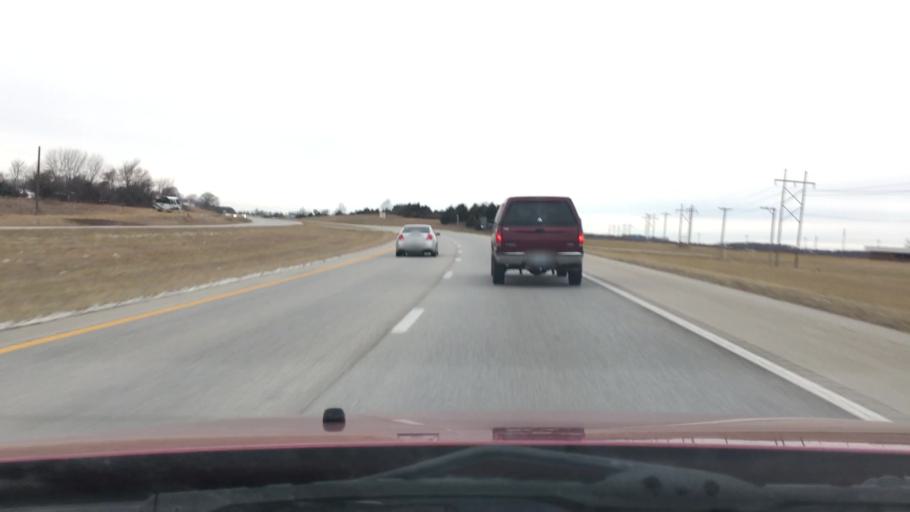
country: US
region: Missouri
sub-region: Webster County
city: Seymour
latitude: 37.1561
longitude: -92.7617
